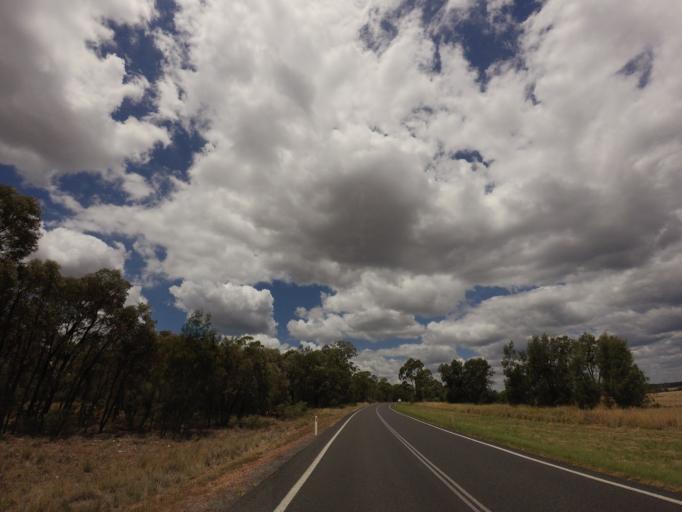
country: AU
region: Queensland
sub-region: Goondiwindi
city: Goondiwindi
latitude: -28.0008
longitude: 150.9026
